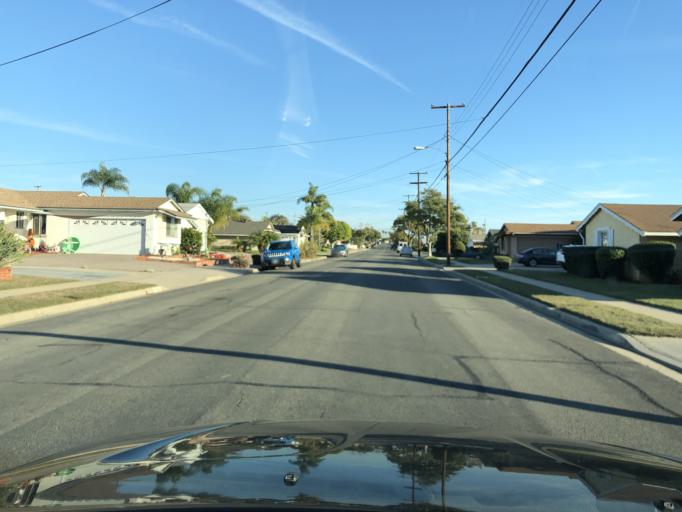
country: US
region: California
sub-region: San Diego County
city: La Jolla
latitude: 32.8245
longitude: -117.1911
